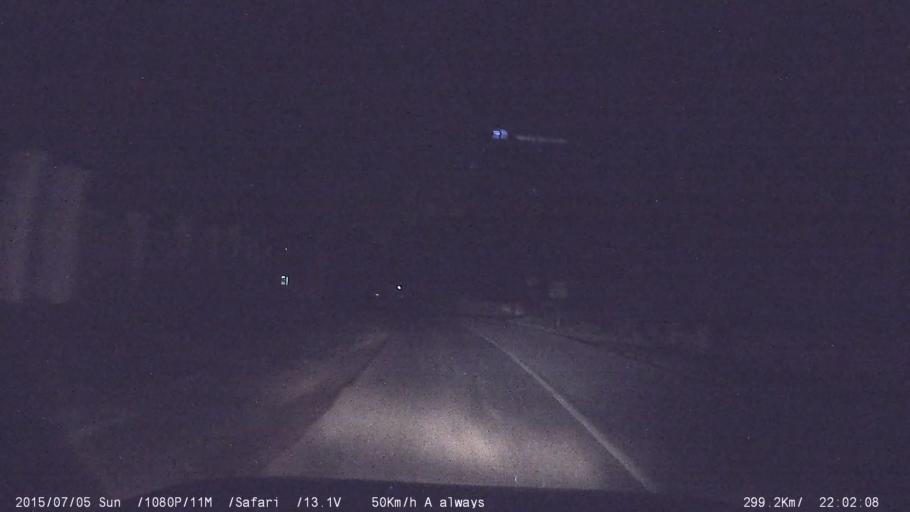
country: IN
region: Kerala
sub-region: Palakkad district
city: Mannarakkat
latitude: 10.9414
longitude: 76.5255
